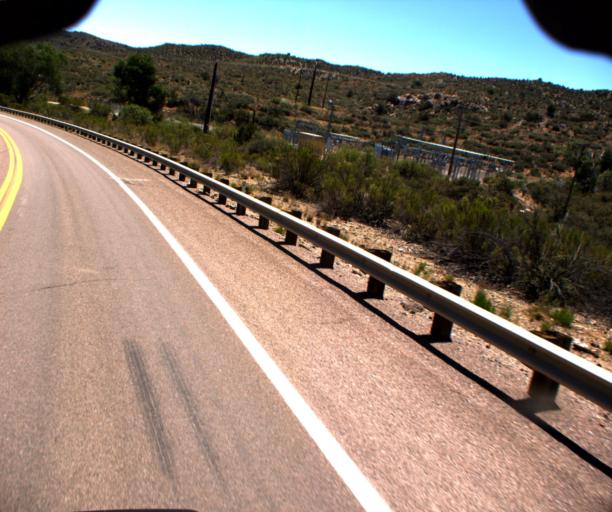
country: US
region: Arizona
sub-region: Yavapai County
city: Bagdad
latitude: 34.5670
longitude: -113.1753
